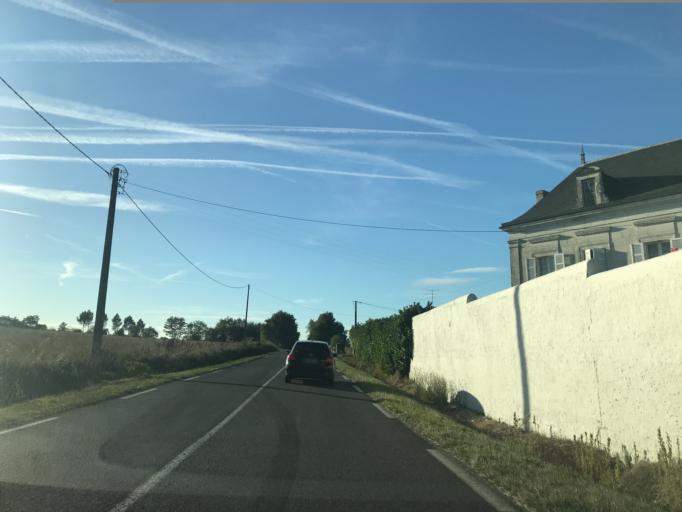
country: FR
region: Poitou-Charentes
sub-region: Departement de la Charente-Maritime
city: Montguyon
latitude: 45.2042
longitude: -0.1503
